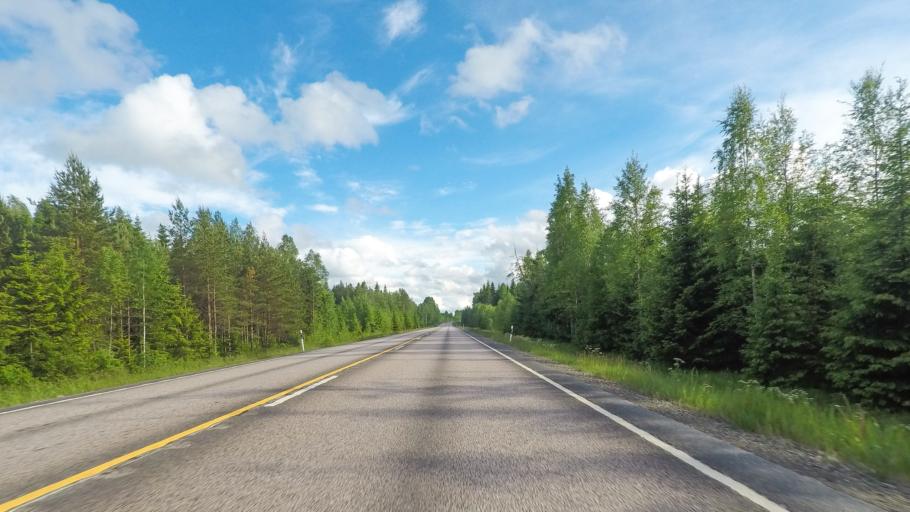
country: FI
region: Central Finland
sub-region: Joutsa
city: Leivonmaeki
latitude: 61.8570
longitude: 26.1025
